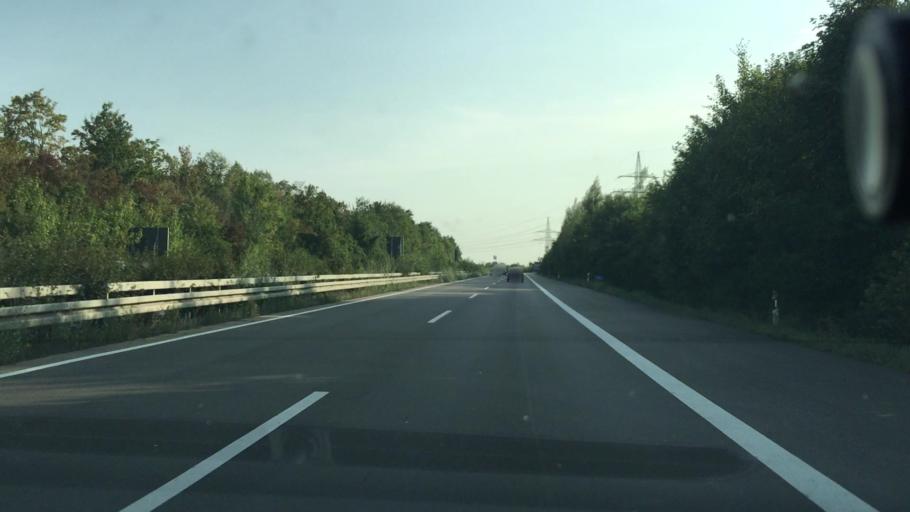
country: DE
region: Lower Saxony
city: Wolfsburg
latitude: 52.4097
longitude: 10.7343
